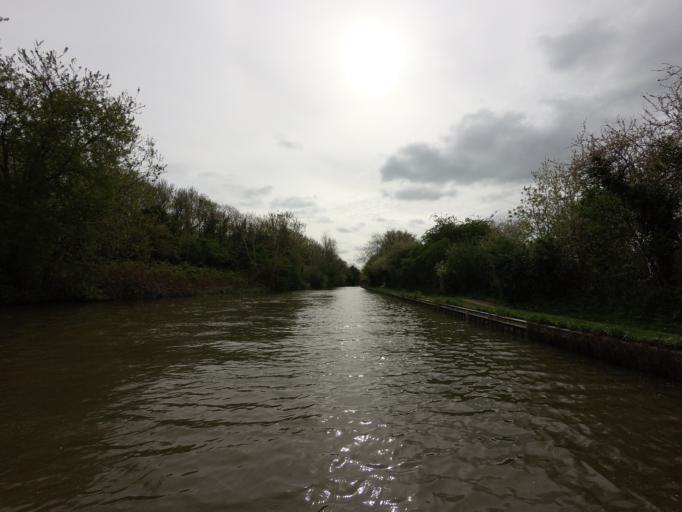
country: GB
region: England
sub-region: Milton Keynes
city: Bradwell
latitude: 52.0660
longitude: -0.7824
